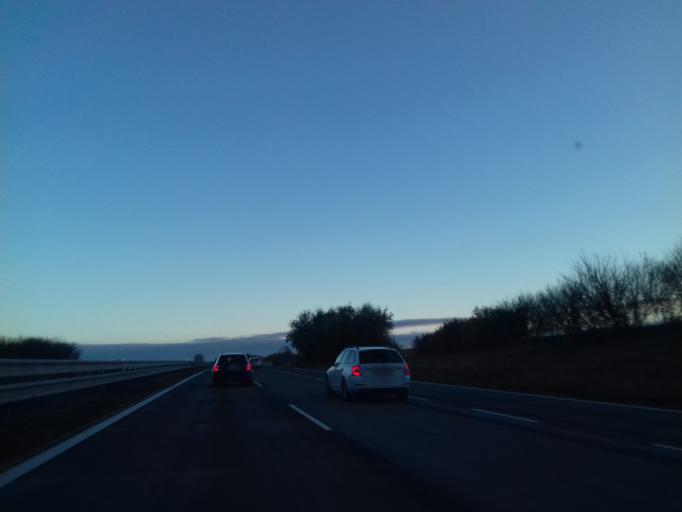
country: CZ
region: South Moravian
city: Rousinov
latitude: 49.2243
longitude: 16.9267
